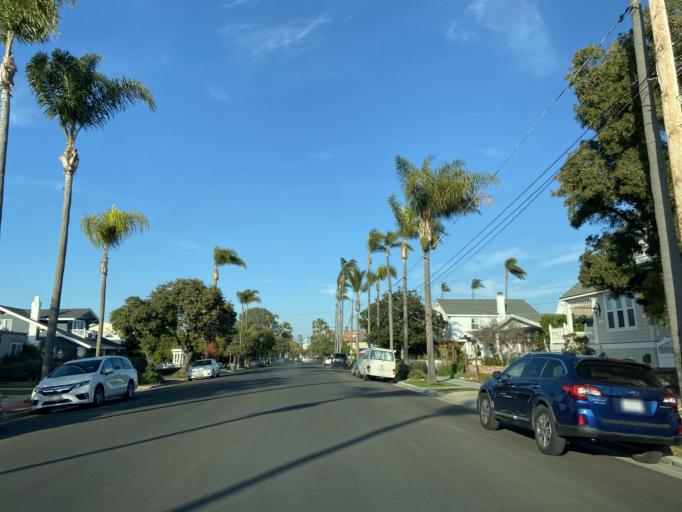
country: US
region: California
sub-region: San Diego County
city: Coronado
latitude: 32.6863
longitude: -117.1754
